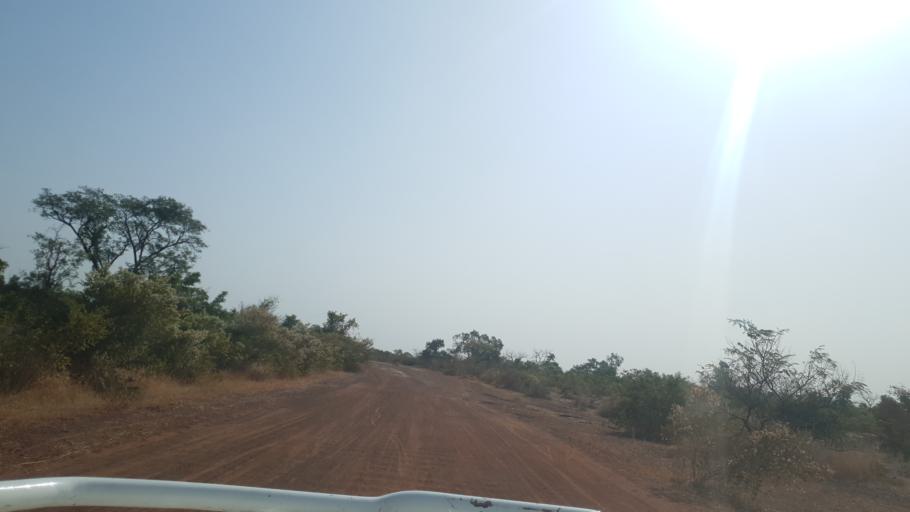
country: ML
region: Koulikoro
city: Dioila
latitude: 12.6678
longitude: -6.7003
